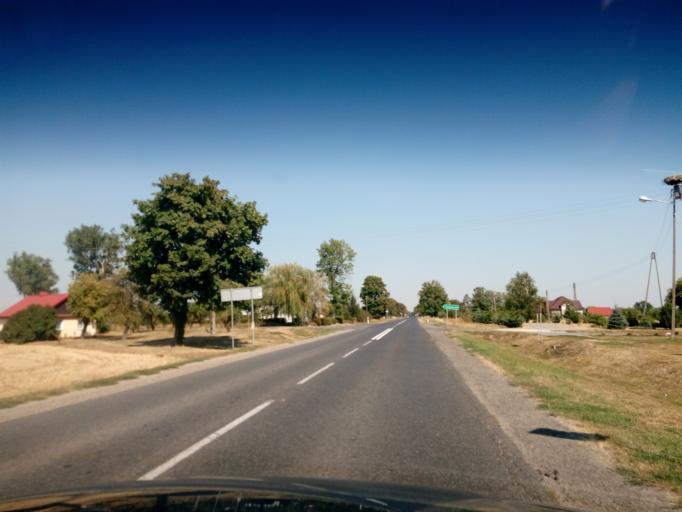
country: PL
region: Lublin Voivodeship
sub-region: Powiat hrubieszowski
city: Hrubieszow
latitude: 50.8231
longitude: 23.9432
